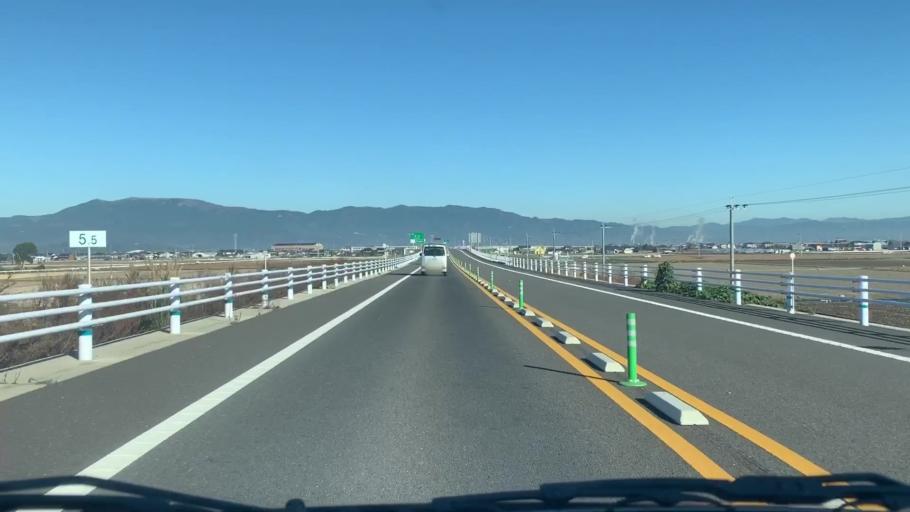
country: JP
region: Saga Prefecture
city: Saga-shi
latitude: 33.2120
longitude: 130.2147
